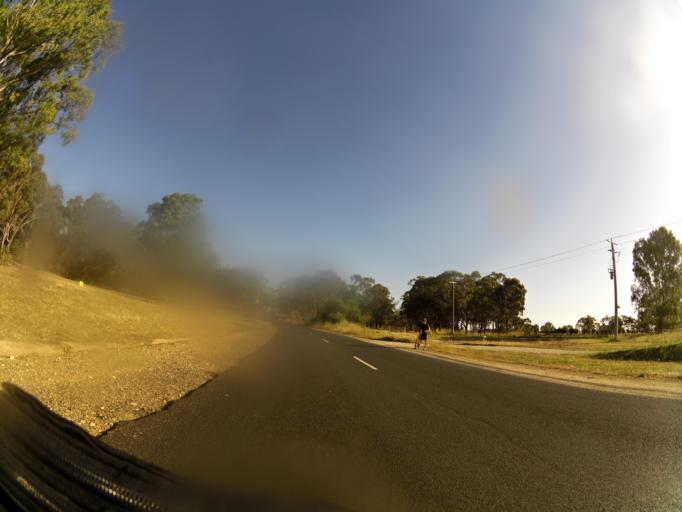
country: AU
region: Victoria
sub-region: Murrindindi
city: Kinglake West
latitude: -37.0282
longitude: 145.1032
